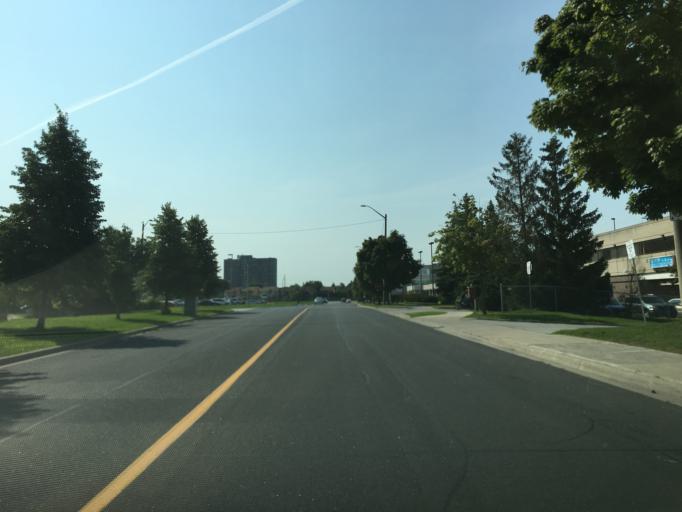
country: CA
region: Ontario
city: Markham
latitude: 43.8209
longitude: -79.3310
